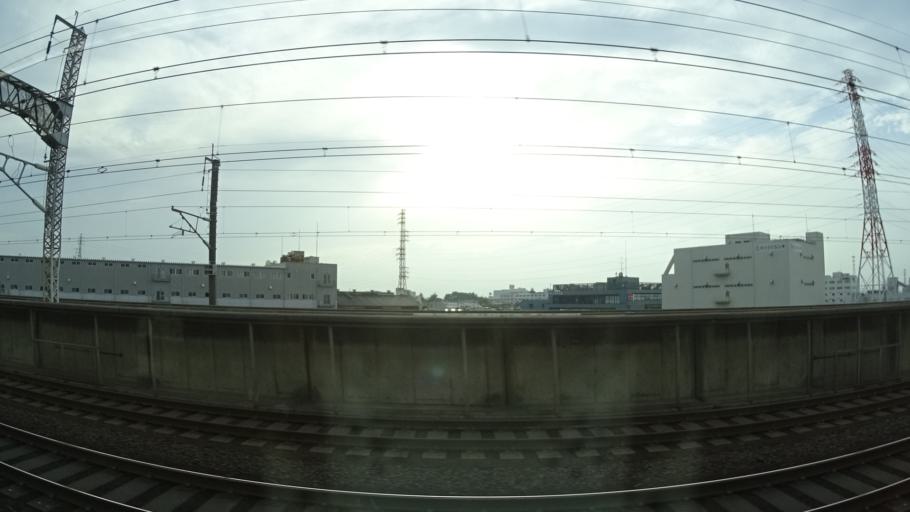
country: JP
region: Saitama
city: Ageoshimo
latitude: 35.9602
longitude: 139.6217
